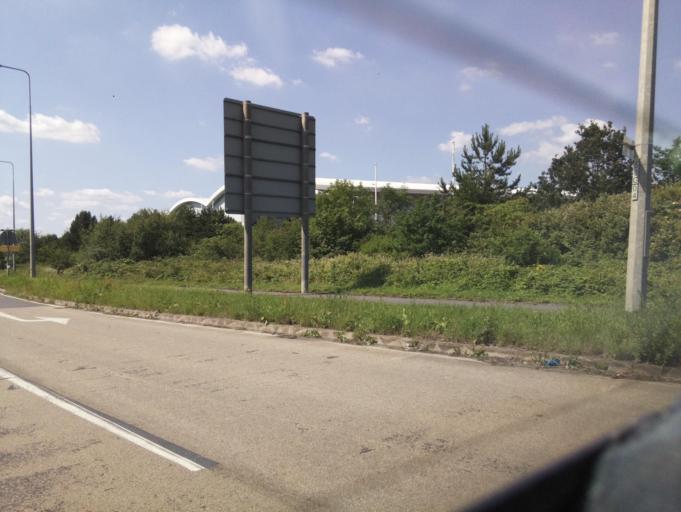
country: GB
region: England
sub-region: Leicestershire
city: Hinckley
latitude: 52.5254
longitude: -1.3882
